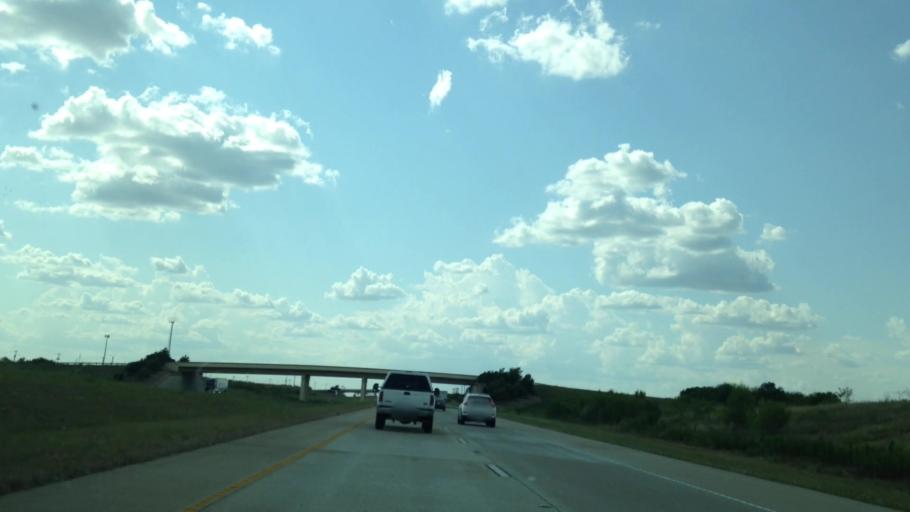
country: US
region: Texas
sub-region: Travis County
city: Onion Creek
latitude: 30.0918
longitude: -97.7533
